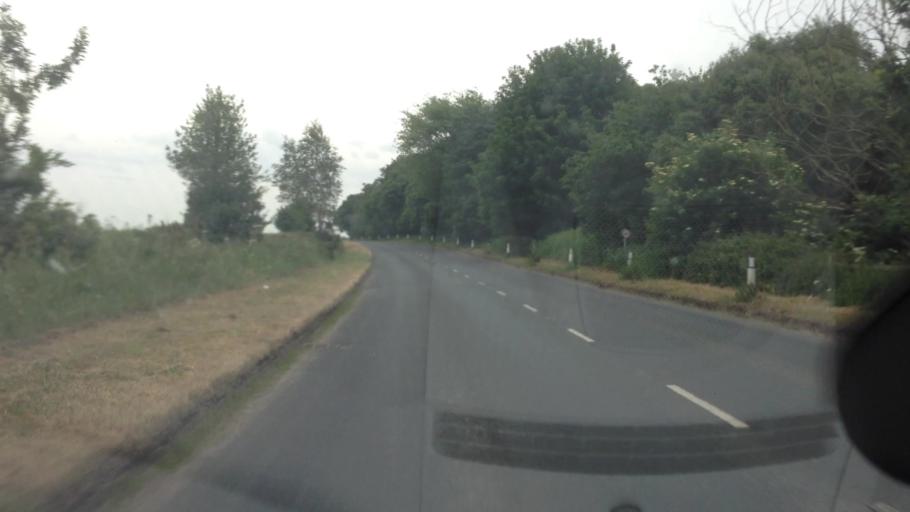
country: GB
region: England
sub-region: City and Borough of Wakefield
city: Woolley
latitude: 53.6120
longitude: -1.5343
